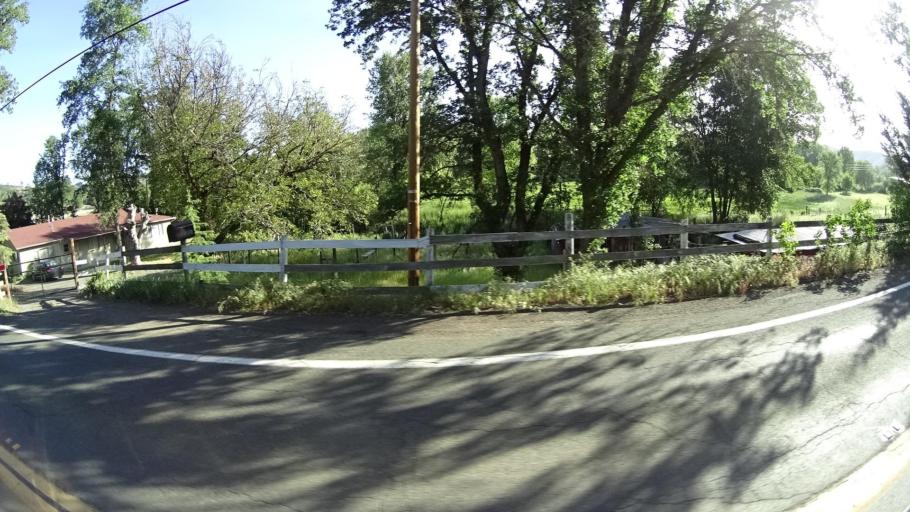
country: US
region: California
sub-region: Lake County
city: North Lakeport
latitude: 39.0955
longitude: -122.9683
